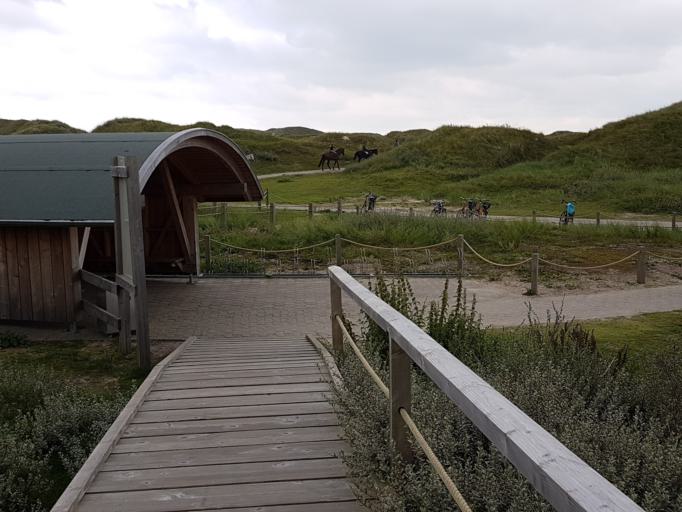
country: DE
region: Lower Saxony
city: Norderney
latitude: 53.7191
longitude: 7.1940
